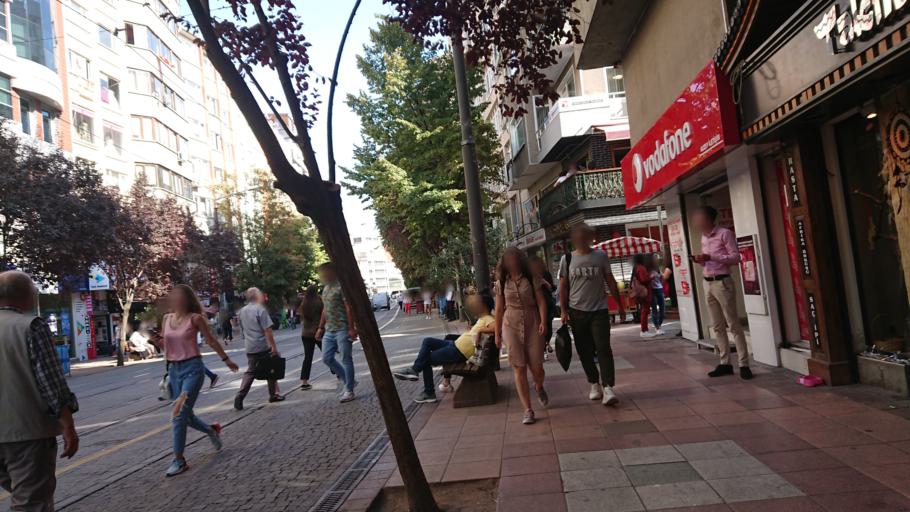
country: TR
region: Eskisehir
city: Eskisehir
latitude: 39.7781
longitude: 30.5161
